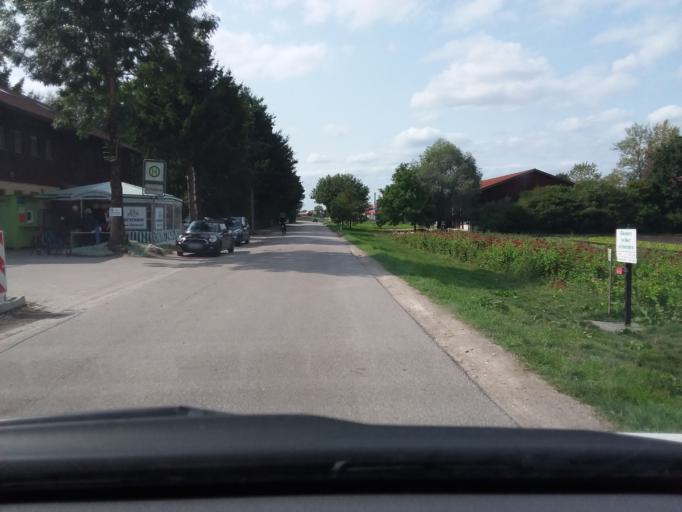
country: DE
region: Bavaria
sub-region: Upper Bavaria
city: Ismaning
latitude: 48.2298
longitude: 11.7025
